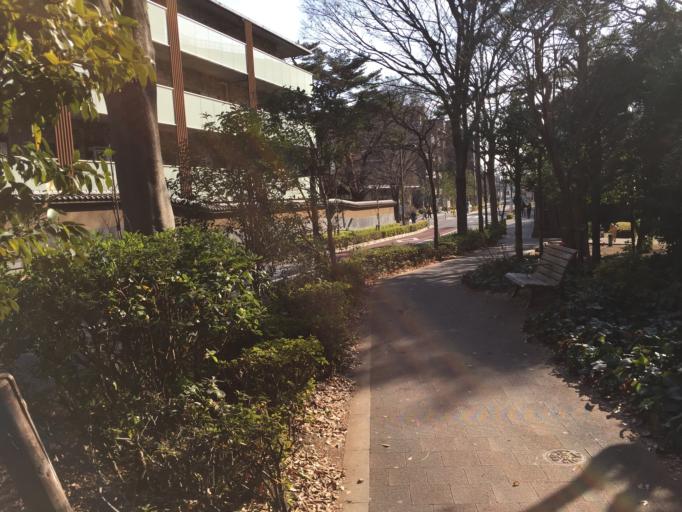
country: JP
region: Tokyo
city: Mitaka-shi
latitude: 35.6676
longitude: 139.6083
